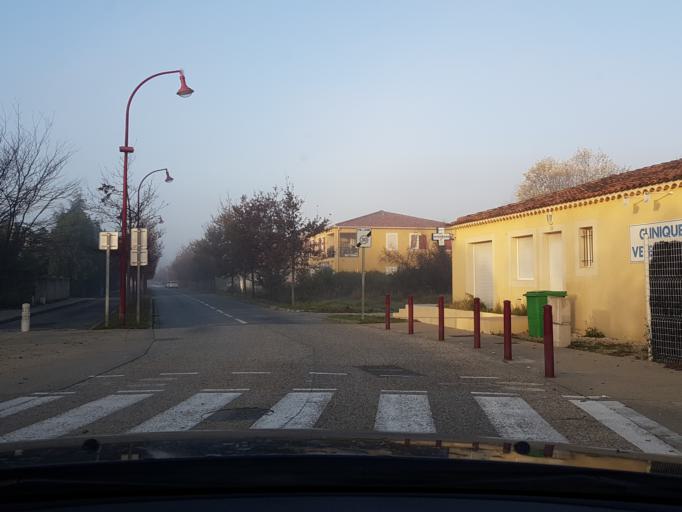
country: FR
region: Provence-Alpes-Cote d'Azur
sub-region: Departement du Vaucluse
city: Entraigues-sur-la-Sorgue
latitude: 44.0039
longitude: 4.9144
